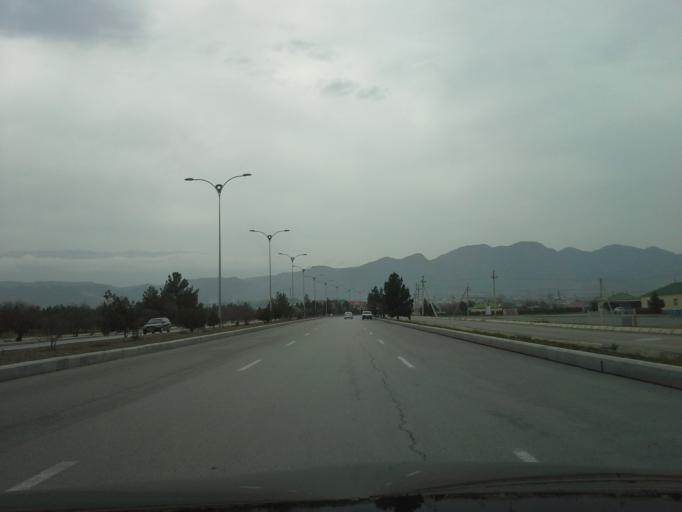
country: TM
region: Ahal
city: Abadan
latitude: 37.9688
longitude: 58.2308
